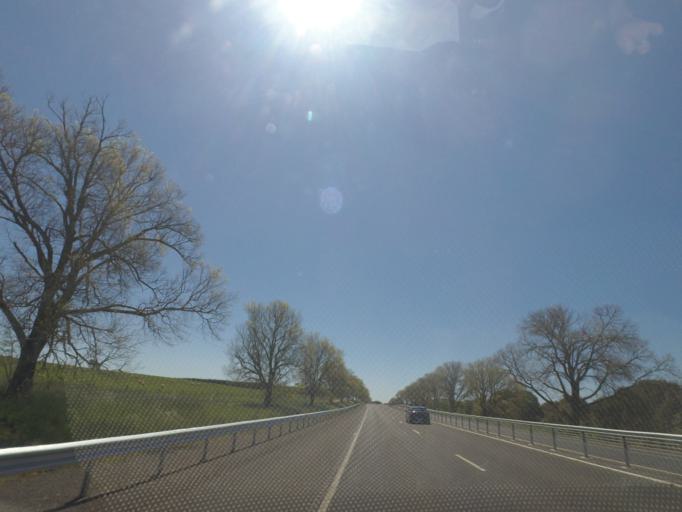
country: AU
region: Victoria
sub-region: Hume
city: Sunbury
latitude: -37.3089
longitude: 144.7388
